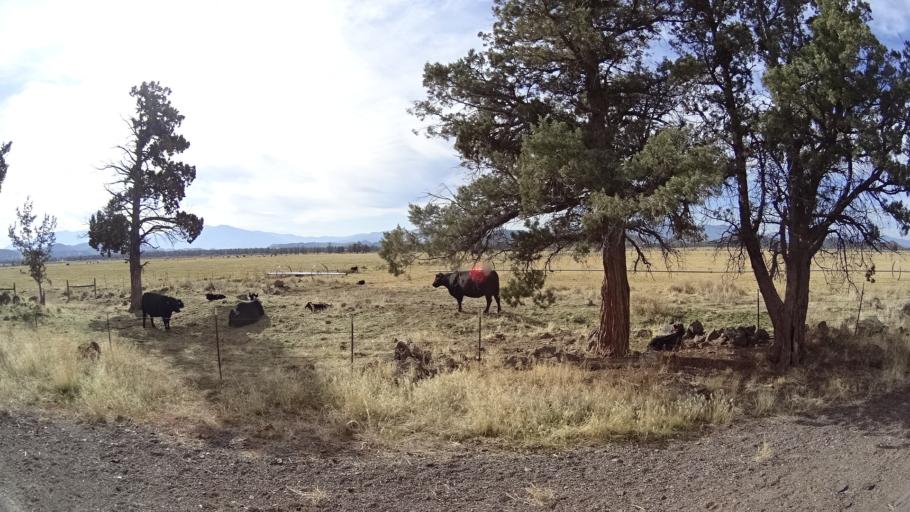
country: US
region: California
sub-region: Siskiyou County
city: Montague
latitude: 41.6050
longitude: -122.4050
